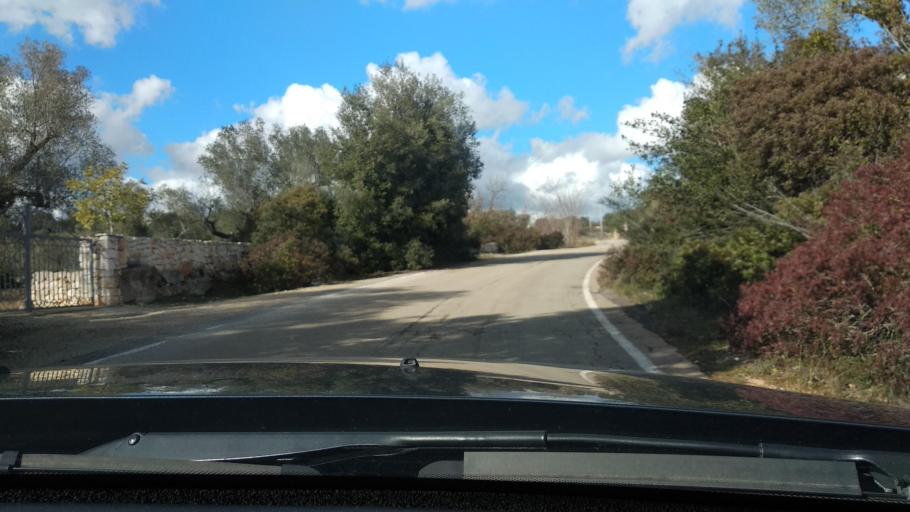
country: IT
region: Apulia
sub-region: Provincia di Brindisi
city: Casalini
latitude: 40.6921
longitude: 17.4739
